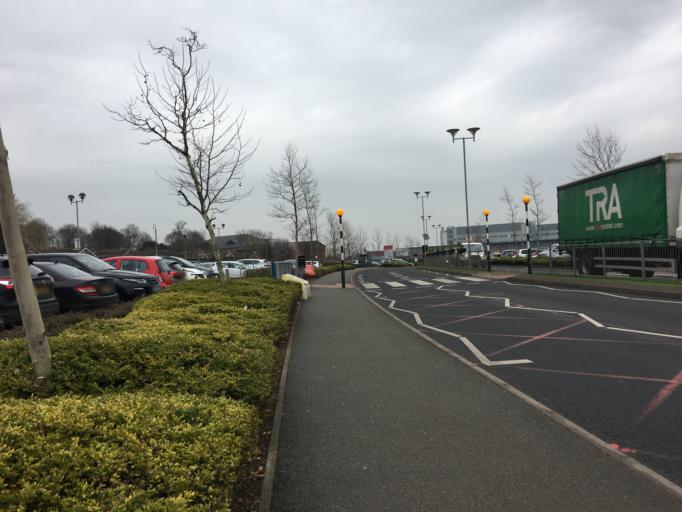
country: GB
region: England
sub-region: Warwickshire
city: Ryton on Dunsmore
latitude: 52.4219
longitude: -1.4426
